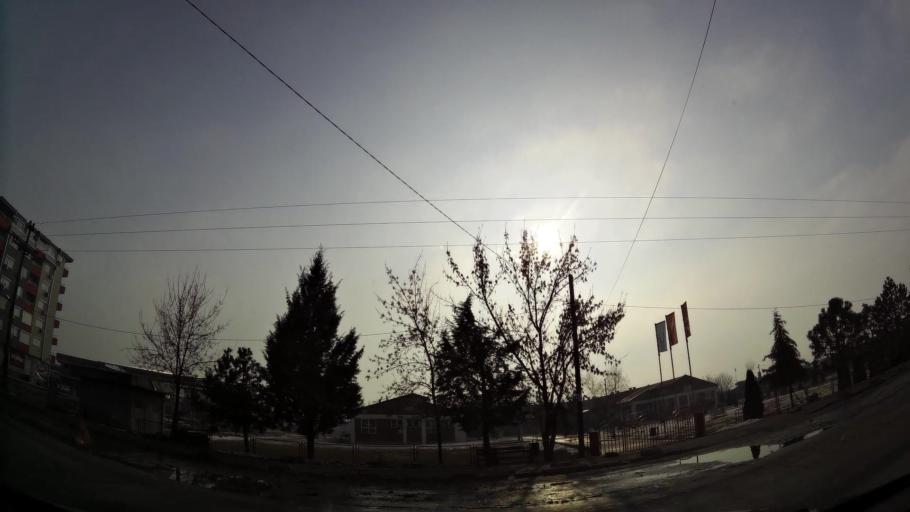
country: MK
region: Ilinden
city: Ilinden
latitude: 41.9910
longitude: 21.5848
